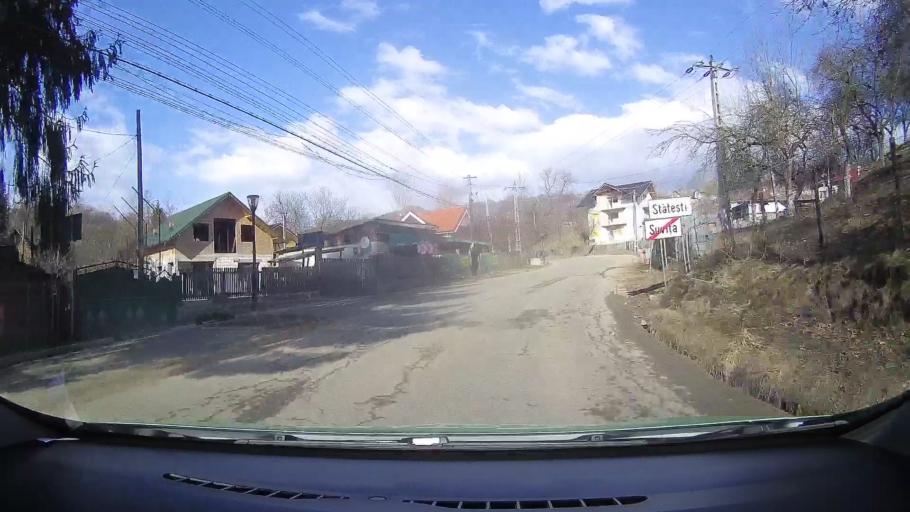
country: RO
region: Dambovita
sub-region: Comuna Varfuri
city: Varfuri
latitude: 45.0884
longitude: 25.4955
